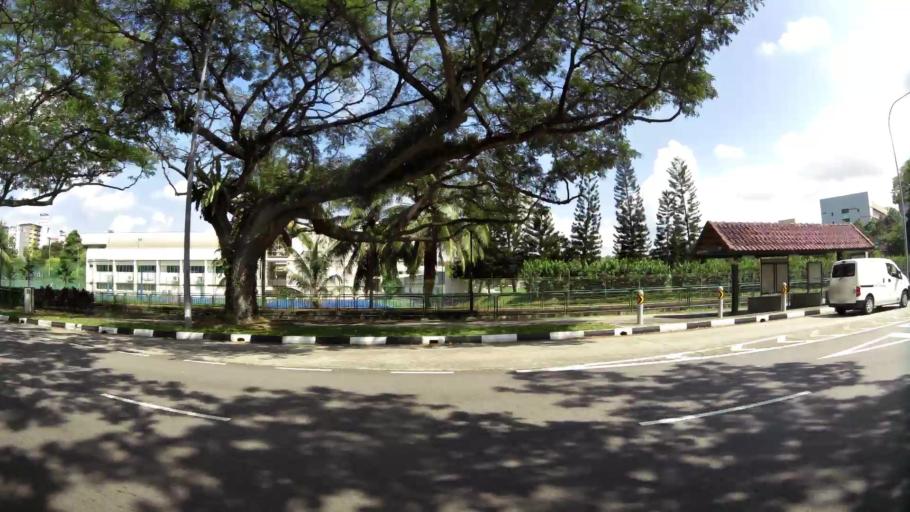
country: SG
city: Singapore
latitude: 1.3772
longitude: 103.8461
